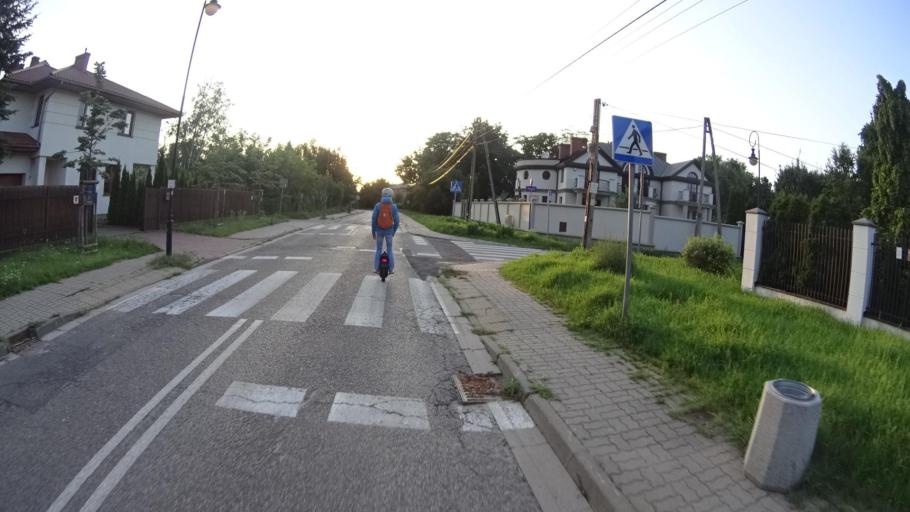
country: PL
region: Masovian Voivodeship
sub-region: Warszawa
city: Bielany
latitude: 52.3069
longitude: 20.9367
